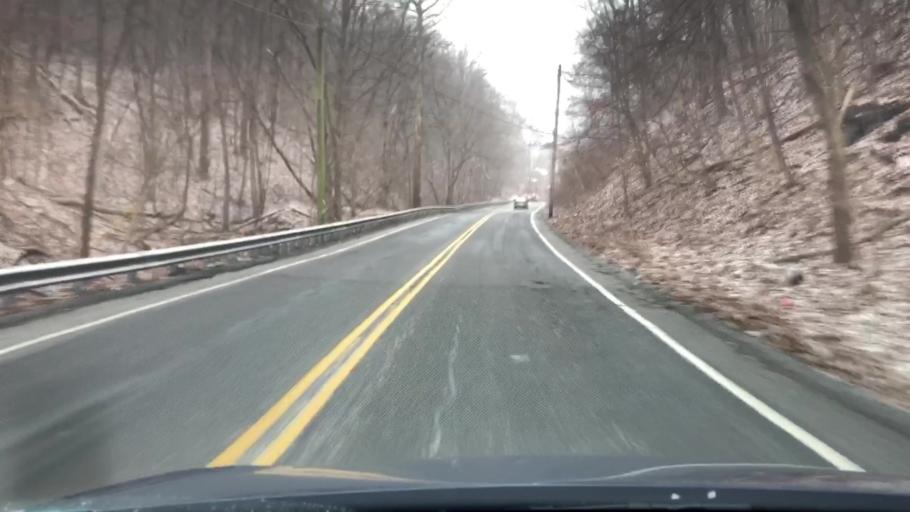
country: US
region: Pennsylvania
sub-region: Allegheny County
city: Blawnox
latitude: 40.4792
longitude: -79.8726
